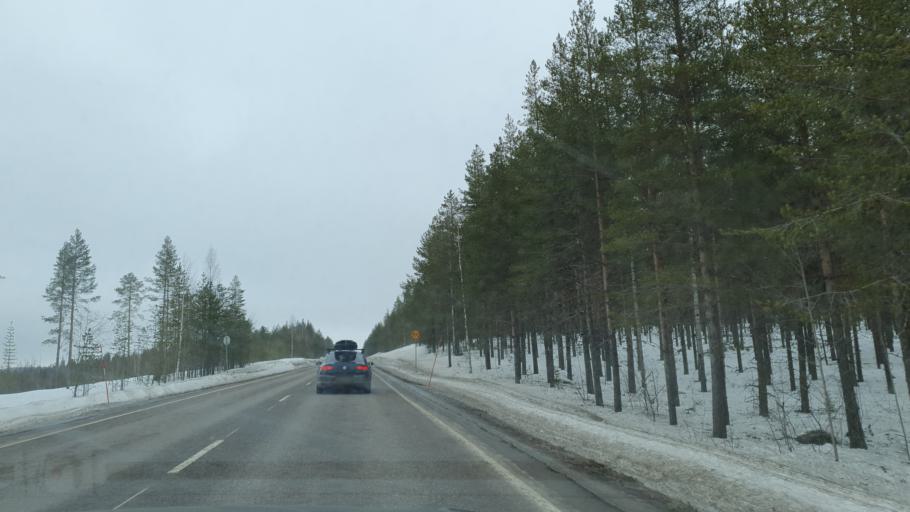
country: FI
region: Lapland
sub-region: Torniolaakso
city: Pello
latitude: 66.8555
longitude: 24.0460
